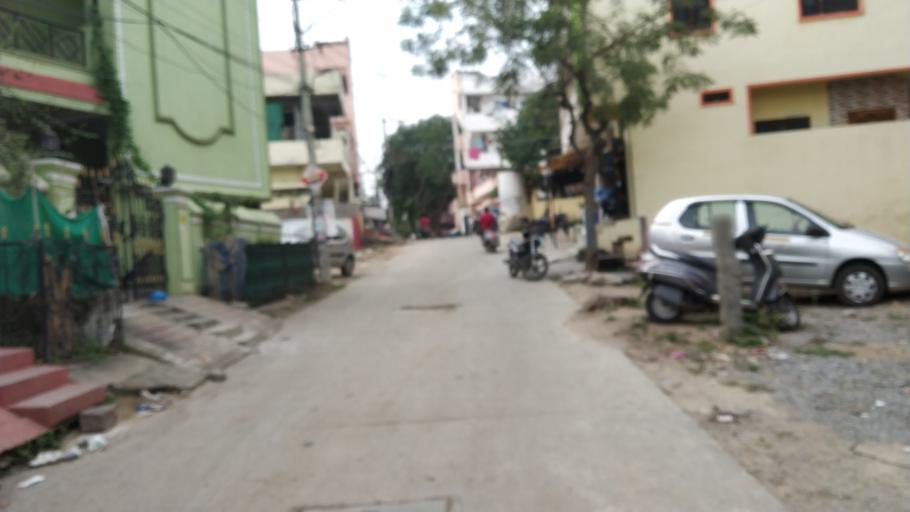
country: IN
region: Telangana
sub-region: Hyderabad
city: Malkajgiri
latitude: 17.4612
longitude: 78.5652
